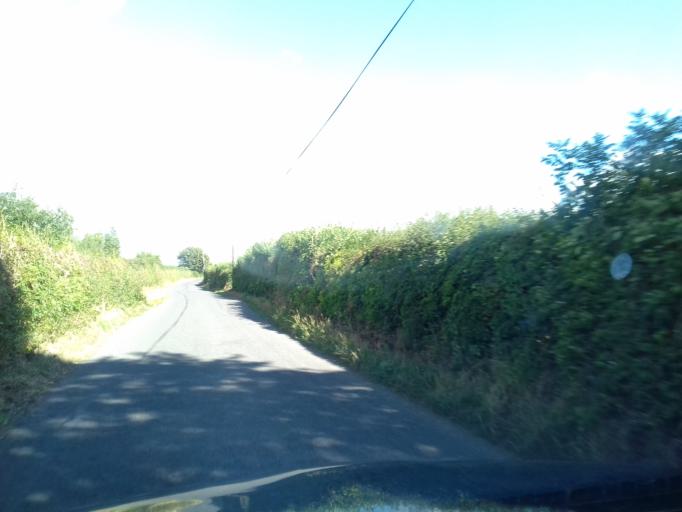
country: IE
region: Leinster
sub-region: Kilkenny
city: Callan
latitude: 52.5393
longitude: -7.3144
